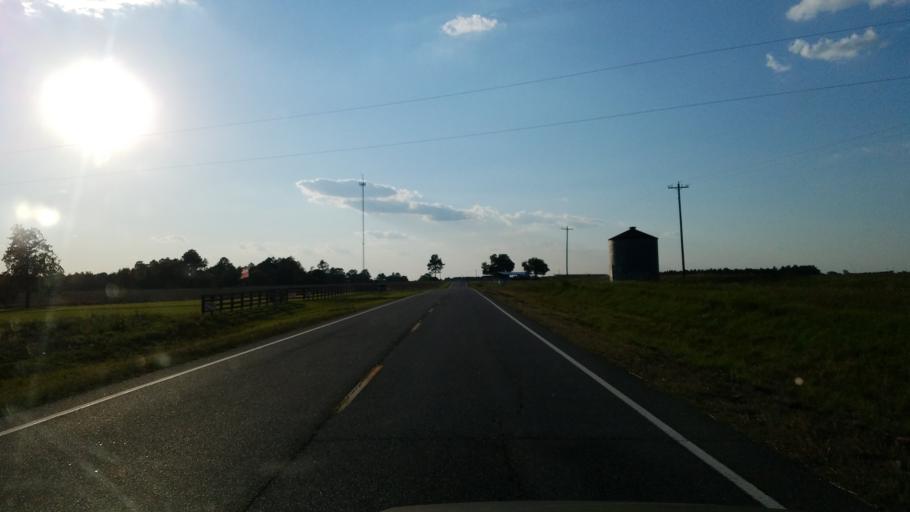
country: US
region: Georgia
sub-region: Berrien County
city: Nashville
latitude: 31.2831
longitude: -83.3358
